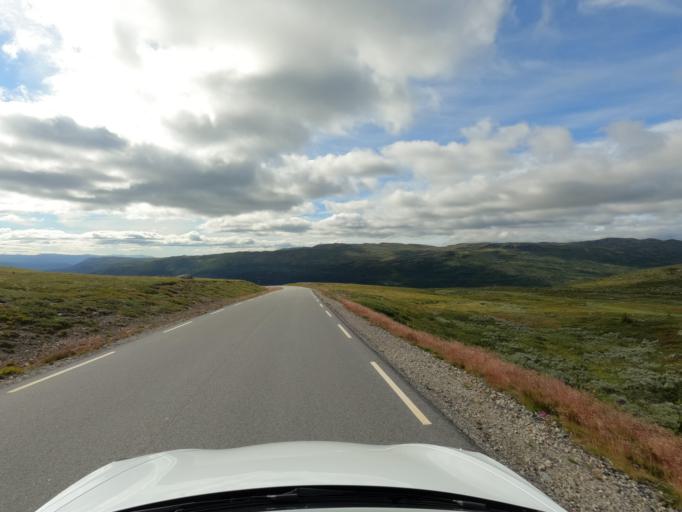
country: NO
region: Telemark
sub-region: Tinn
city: Rjukan
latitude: 60.1568
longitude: 8.6103
